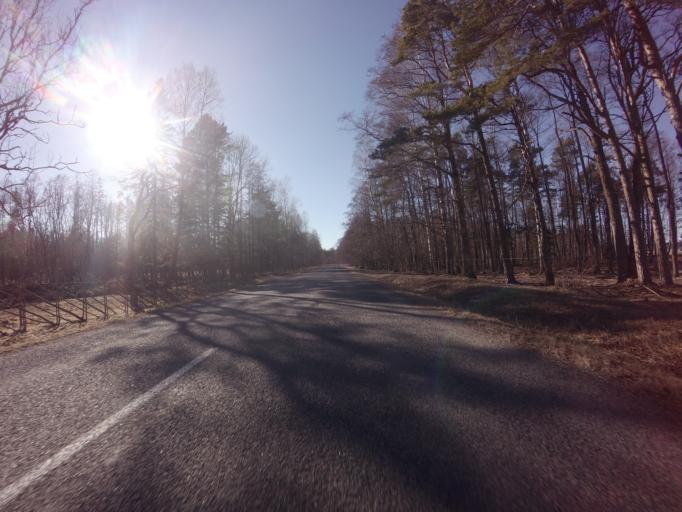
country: EE
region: Saare
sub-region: Kuressaare linn
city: Kuressaare
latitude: 58.4856
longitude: 22.2733
